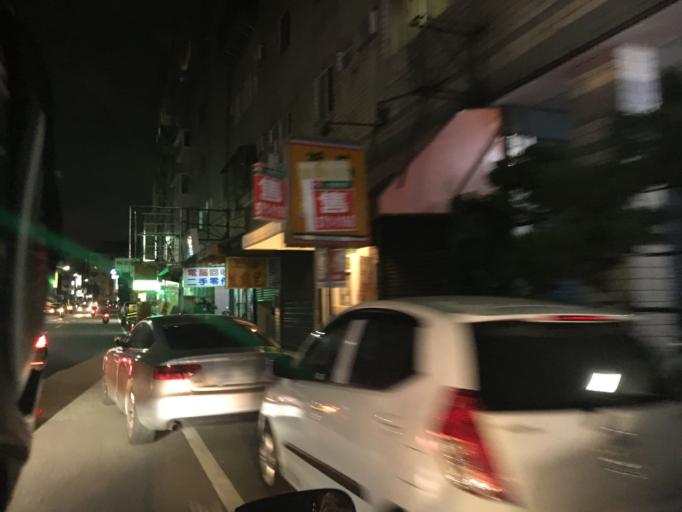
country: TW
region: Taiwan
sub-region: Hsinchu
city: Hsinchu
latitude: 24.7964
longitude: 120.9833
